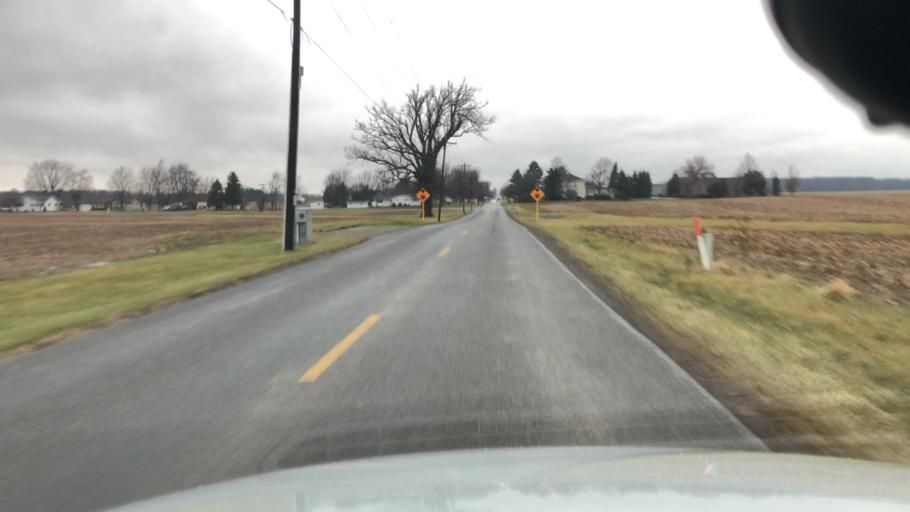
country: US
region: Ohio
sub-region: Allen County
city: Lima
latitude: 40.7871
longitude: -84.0131
